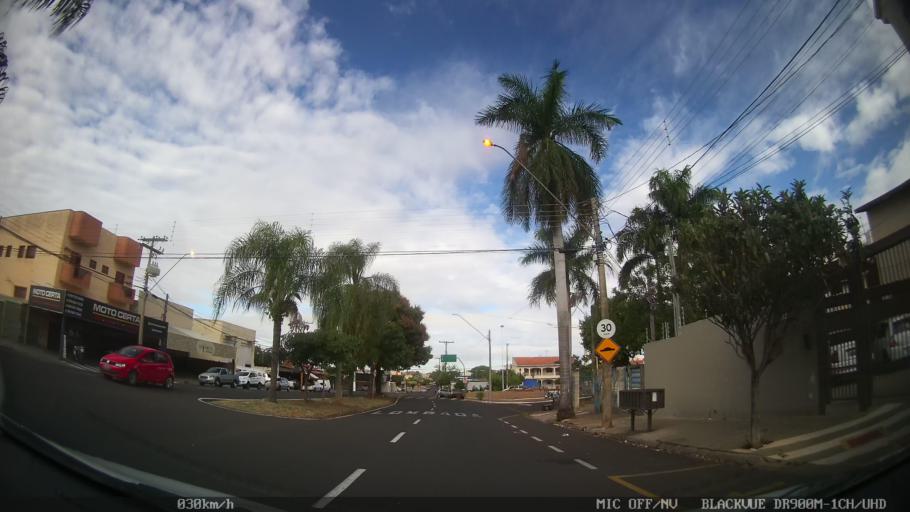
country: BR
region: Sao Paulo
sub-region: Sao Jose Do Rio Preto
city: Sao Jose do Rio Preto
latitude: -20.8415
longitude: -49.3780
